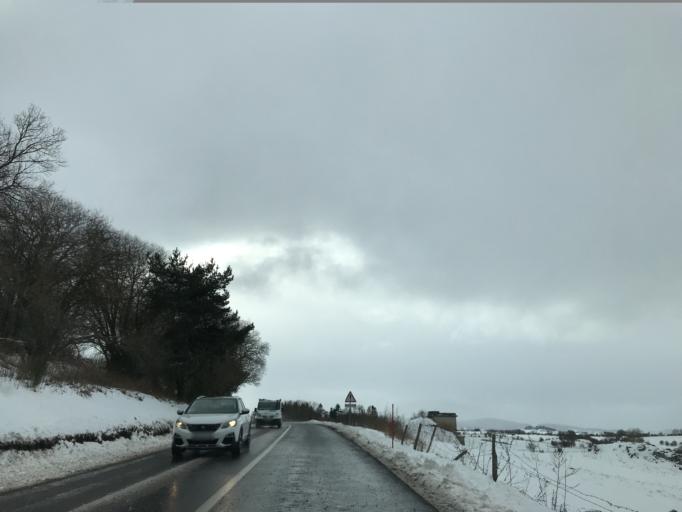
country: FR
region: Auvergne
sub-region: Departement du Puy-de-Dome
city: Aydat
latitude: 45.6837
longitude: 2.9378
